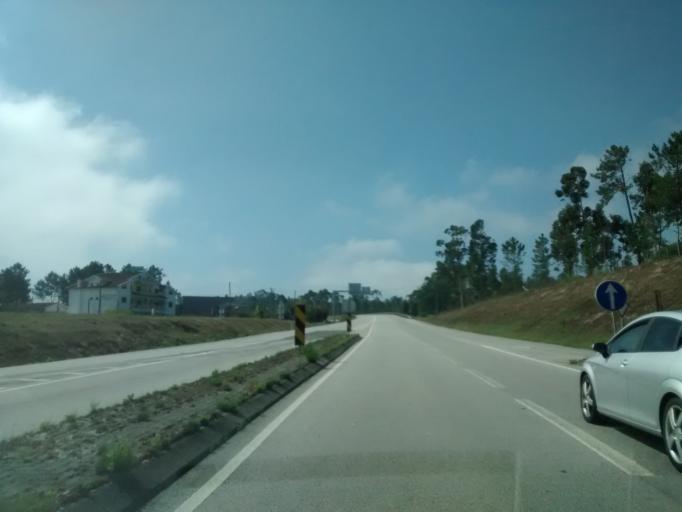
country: PT
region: Aveiro
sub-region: Mealhada
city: Mealhada
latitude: 40.3542
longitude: -8.4517
